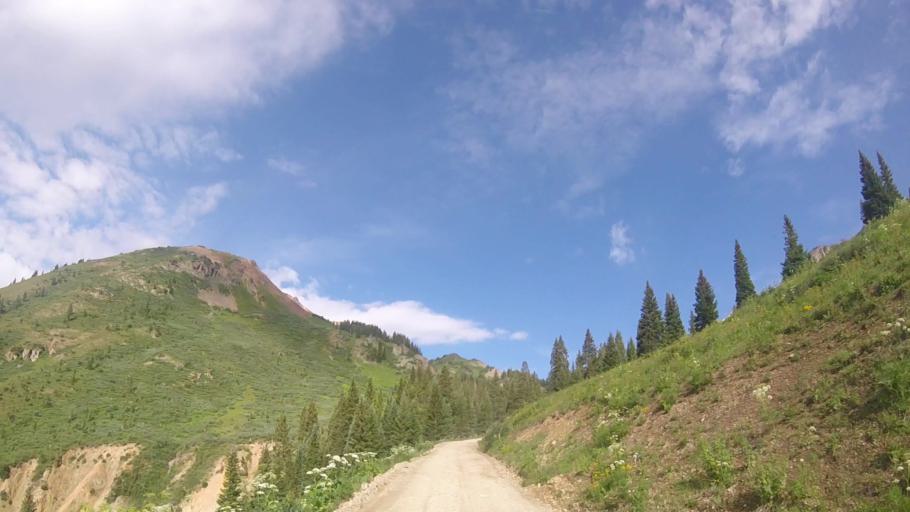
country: US
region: Colorado
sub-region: San Miguel County
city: Telluride
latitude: 37.8461
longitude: -107.7673
